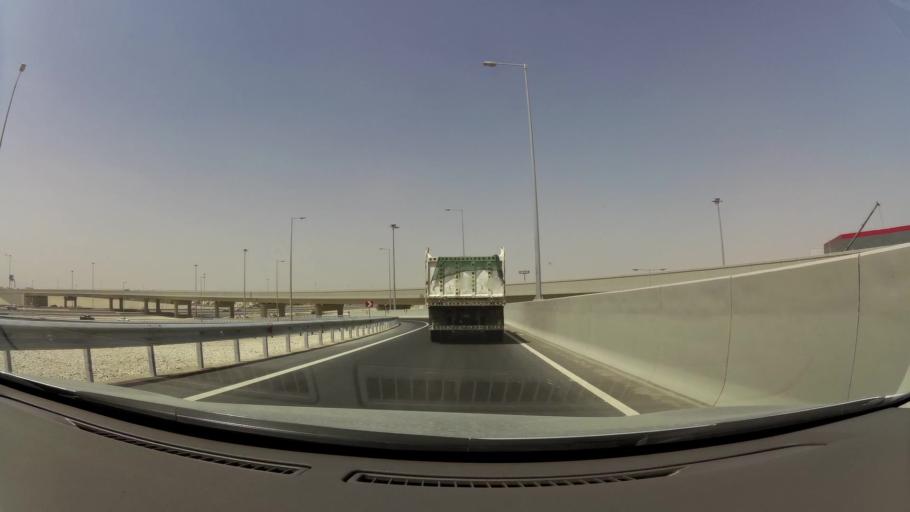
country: QA
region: Baladiyat Umm Salal
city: Umm Salal Muhammad
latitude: 25.3808
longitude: 51.4420
